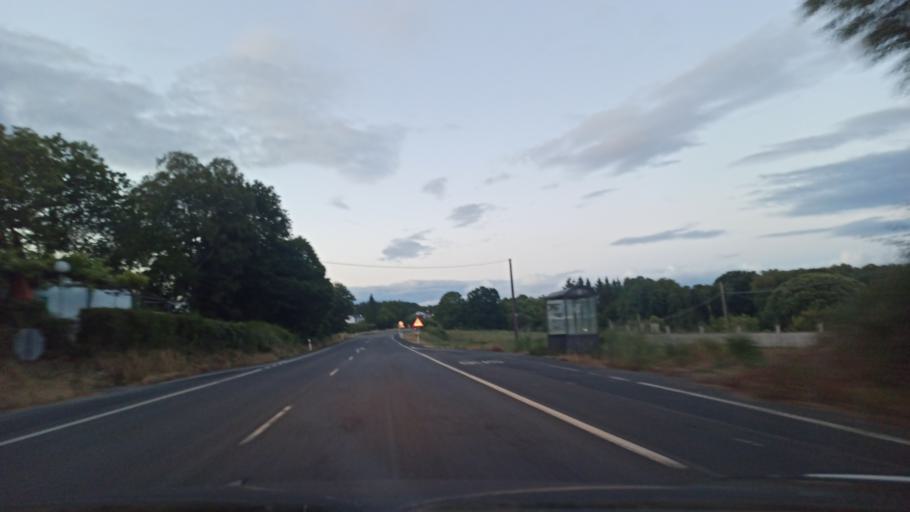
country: ES
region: Galicia
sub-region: Provincia de Lugo
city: Ourol
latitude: 42.9525
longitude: -7.6155
